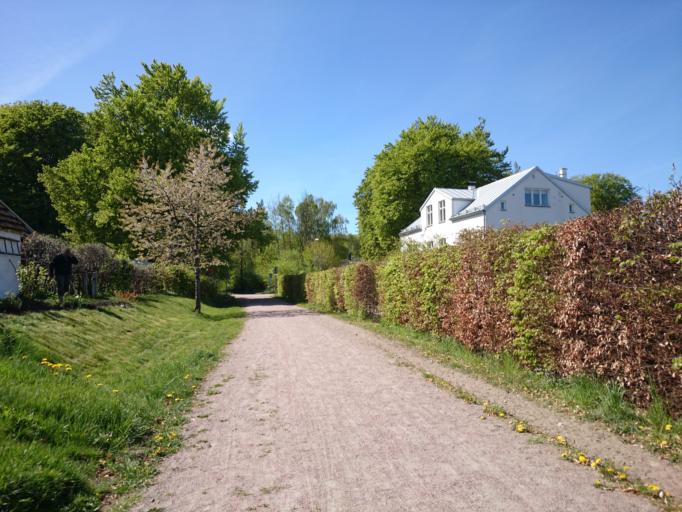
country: SE
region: Skane
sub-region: Lunds Kommun
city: Genarp
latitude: 55.6786
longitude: 13.4126
